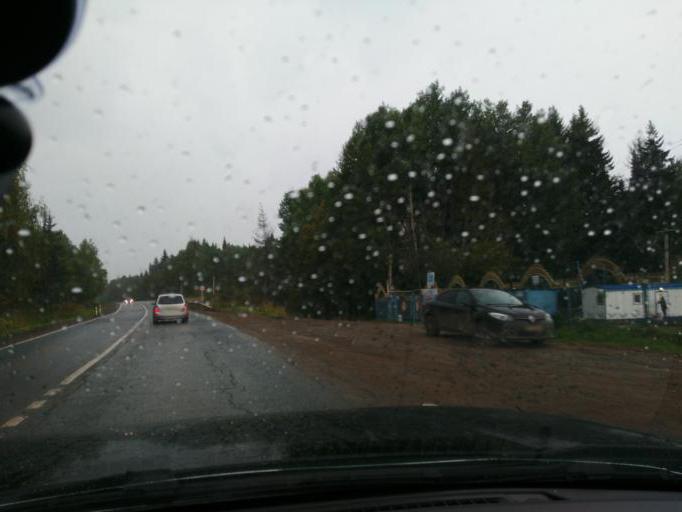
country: RU
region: Perm
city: Barda
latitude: 56.8965
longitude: 55.7404
